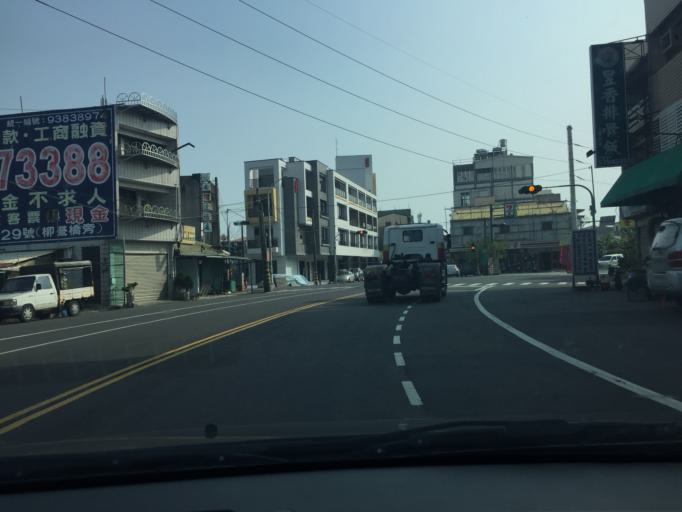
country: TW
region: Taiwan
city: Xinying
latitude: 23.1966
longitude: 120.3181
